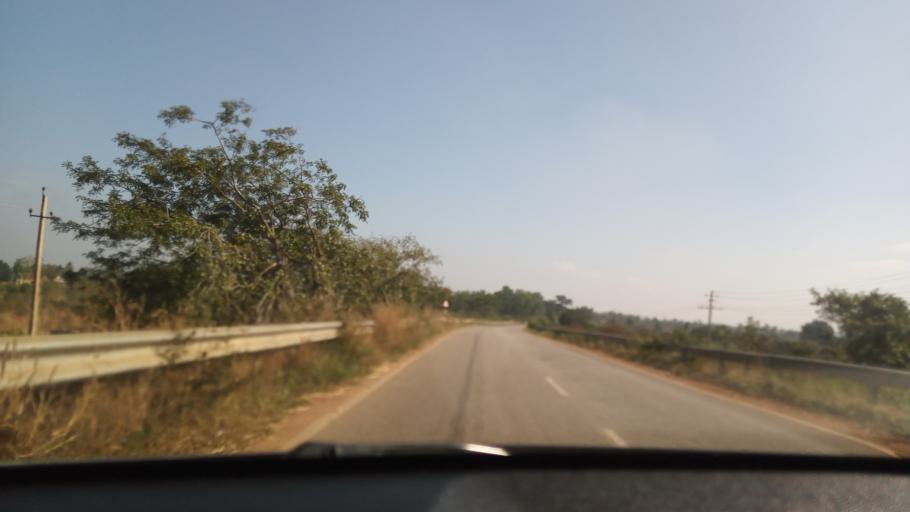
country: IN
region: Karnataka
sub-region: Bangalore Rural
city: Vijayapura
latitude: 13.2779
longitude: 77.7591
